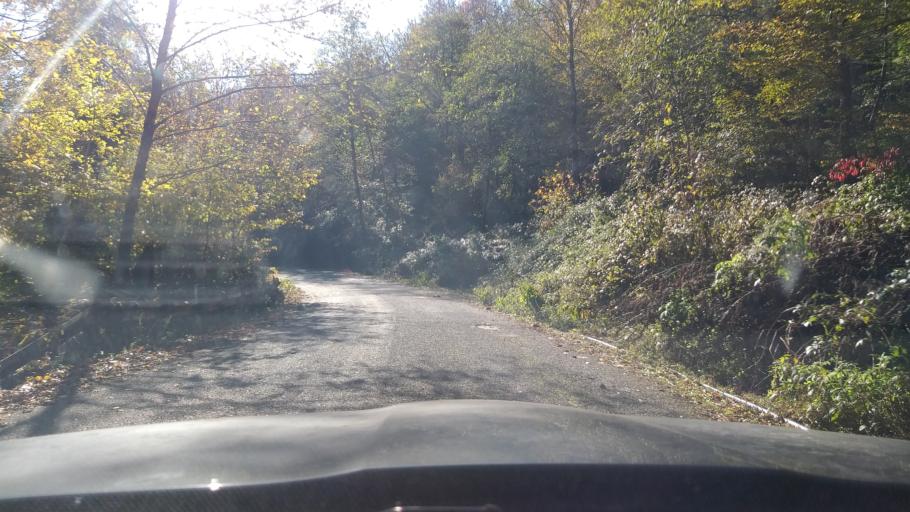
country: GE
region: Abkhazia
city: Bich'vinta
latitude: 43.1833
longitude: 40.4545
